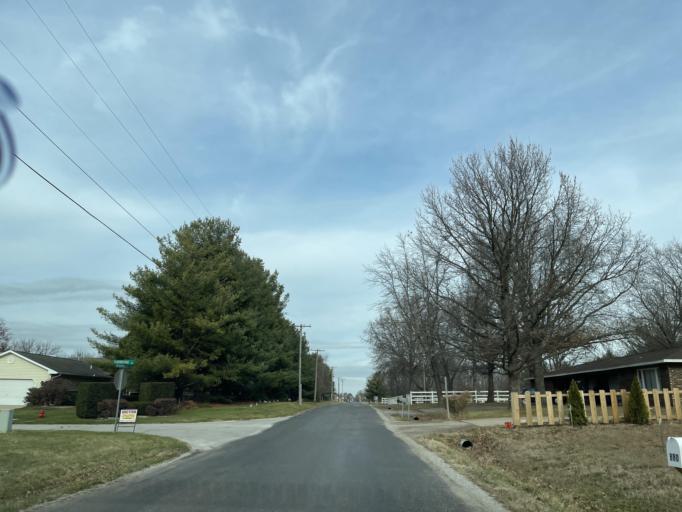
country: US
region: Illinois
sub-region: Sangamon County
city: Leland Grove
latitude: 39.7891
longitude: -89.7296
